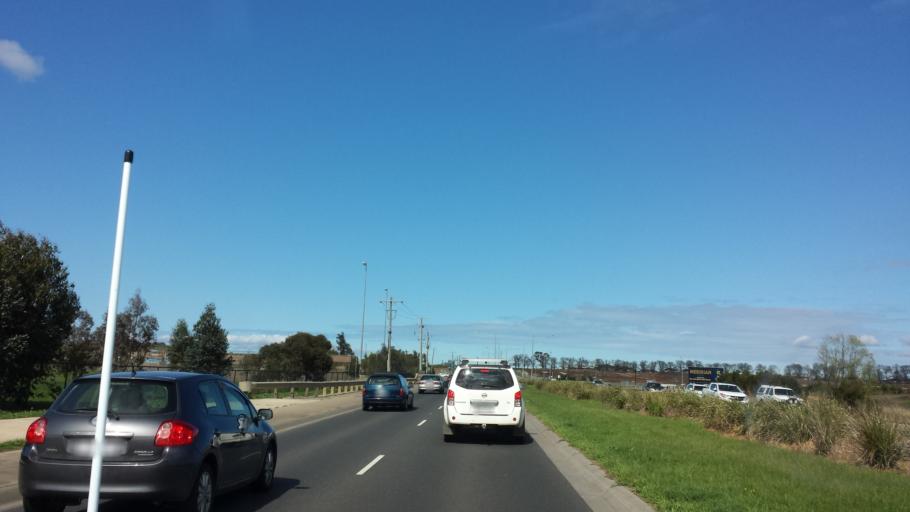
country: AU
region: Victoria
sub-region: Casey
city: Berwick
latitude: -38.0713
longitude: 145.3362
